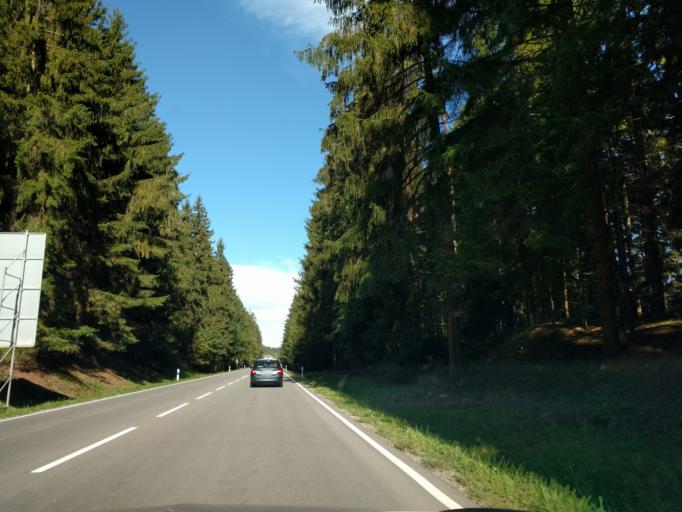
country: DE
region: Bavaria
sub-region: Lower Bavaria
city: Patersdorf
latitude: 49.0295
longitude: 12.9659
